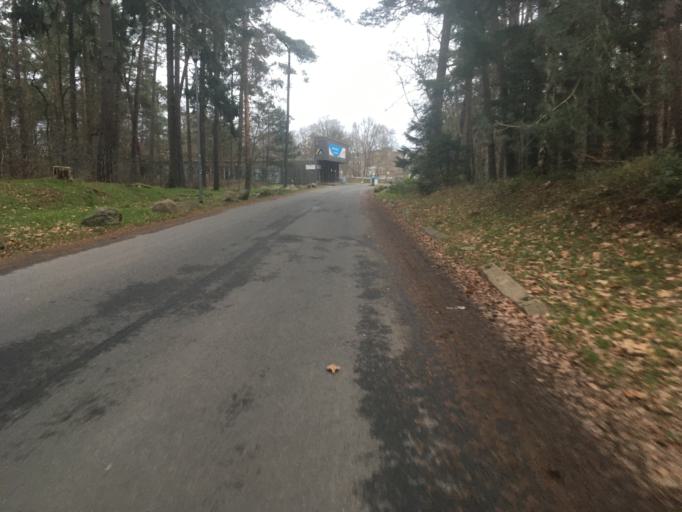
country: DE
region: Mecklenburg-Vorpommern
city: Ostseebad Binz
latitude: 54.4483
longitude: 13.5666
